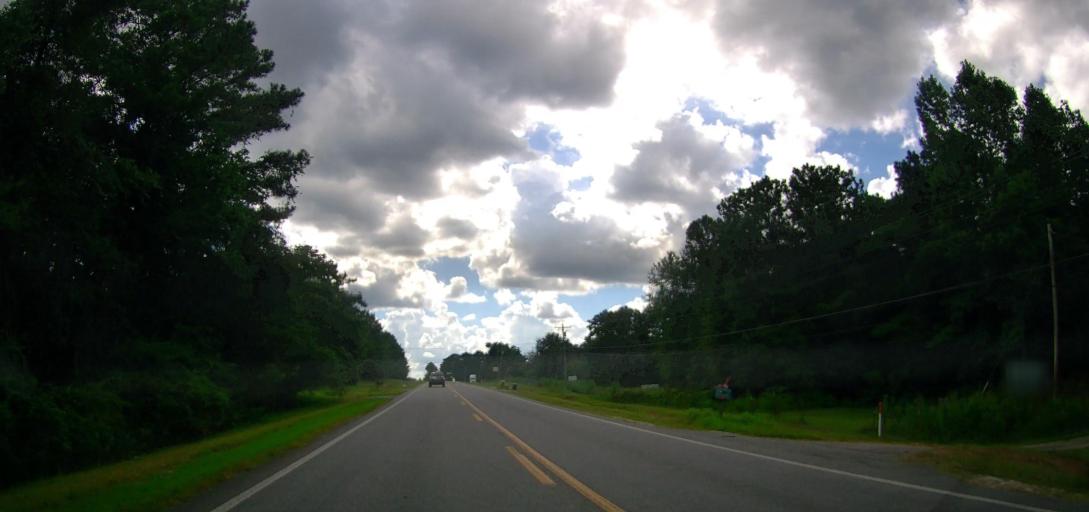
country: US
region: Alabama
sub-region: Russell County
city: Ladonia
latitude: 32.4507
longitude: -85.2277
